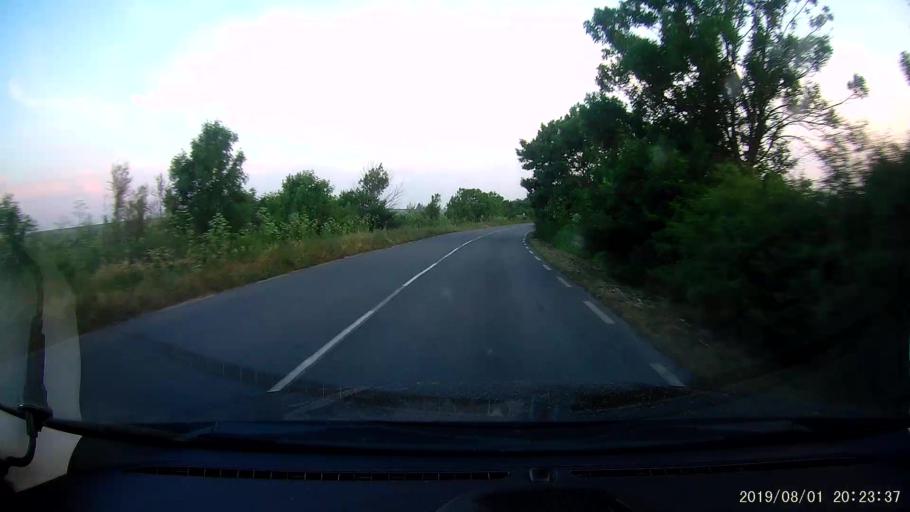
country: BG
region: Yambol
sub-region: Obshtina Elkhovo
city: Elkhovo
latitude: 42.2453
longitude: 26.5989
